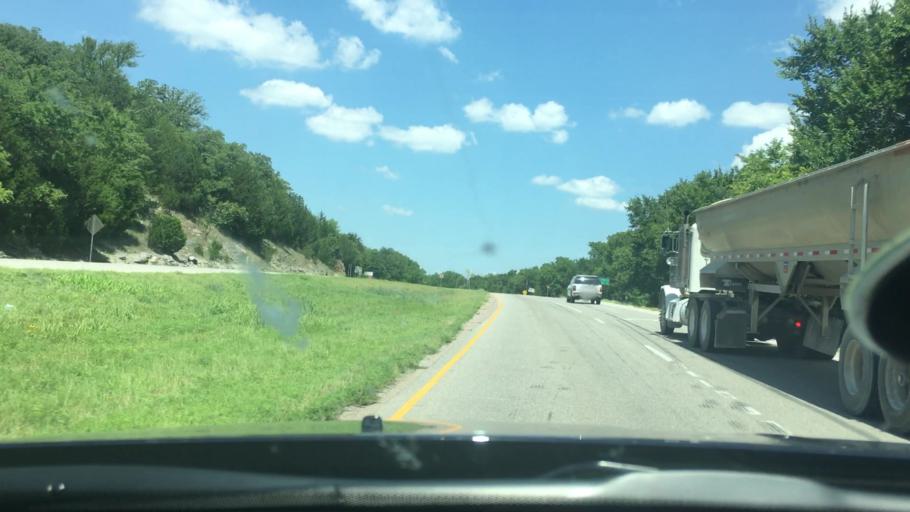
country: US
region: Oklahoma
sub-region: Marshall County
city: Oakland
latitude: 34.1688
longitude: -96.8328
